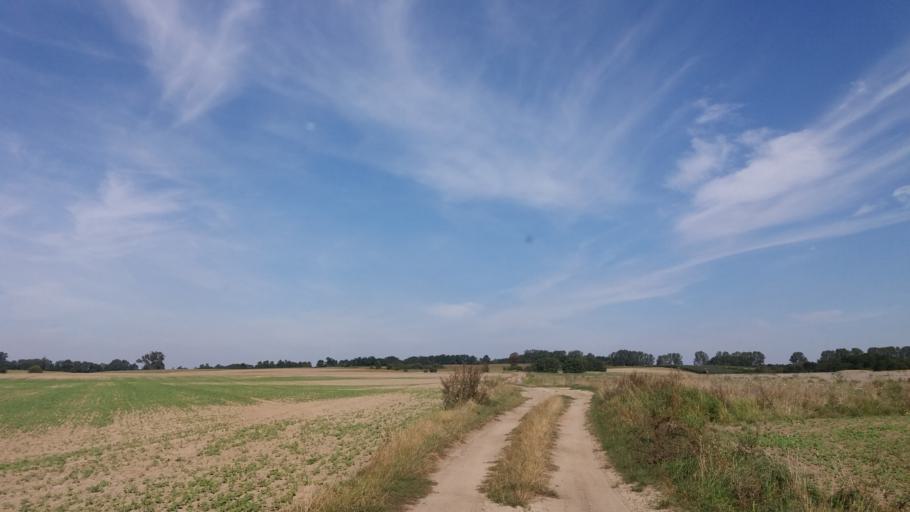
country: PL
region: West Pomeranian Voivodeship
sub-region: Powiat choszczenski
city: Choszczno
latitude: 53.1120
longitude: 15.4108
